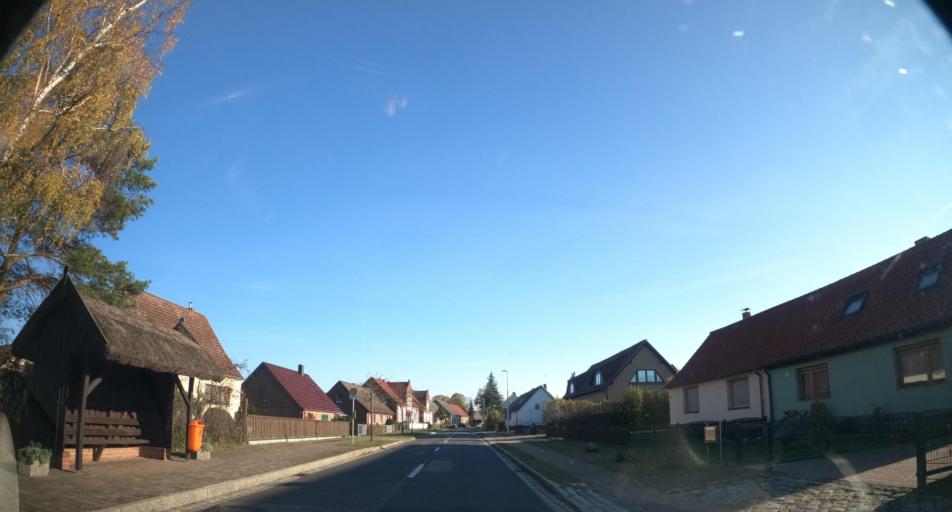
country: DE
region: Mecklenburg-Vorpommern
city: Ahlbeck
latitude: 53.6709
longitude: 14.1820
